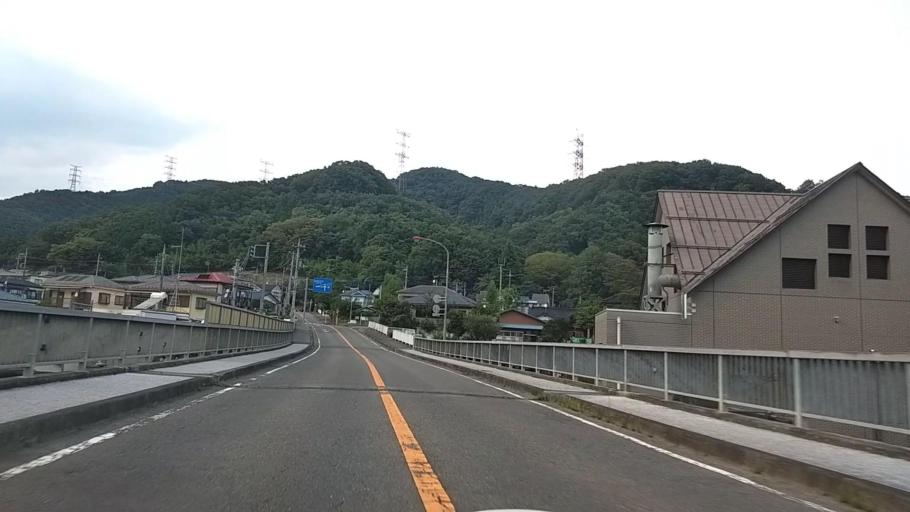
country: JP
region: Yamanashi
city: Uenohara
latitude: 35.6111
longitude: 139.2161
